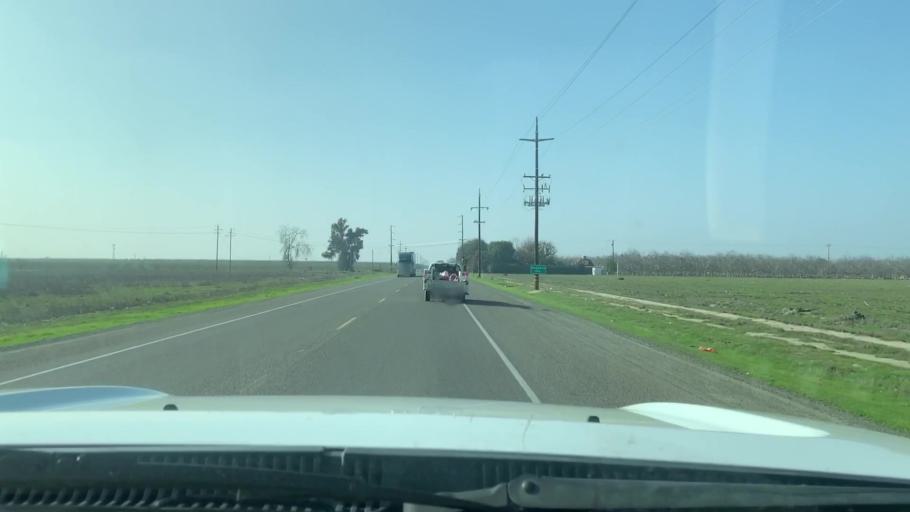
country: US
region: California
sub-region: Kern County
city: Wasco
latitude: 35.6016
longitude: -119.3641
